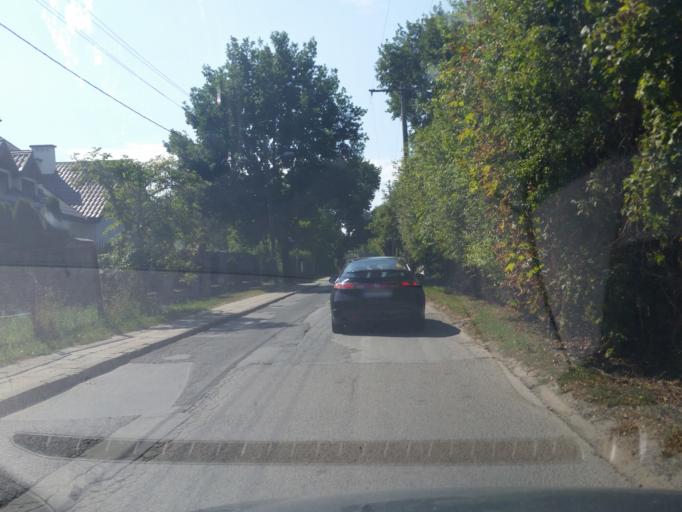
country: PL
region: Masovian Voivodeship
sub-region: Warszawa
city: Bialoleka
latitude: 52.3225
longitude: 20.9756
